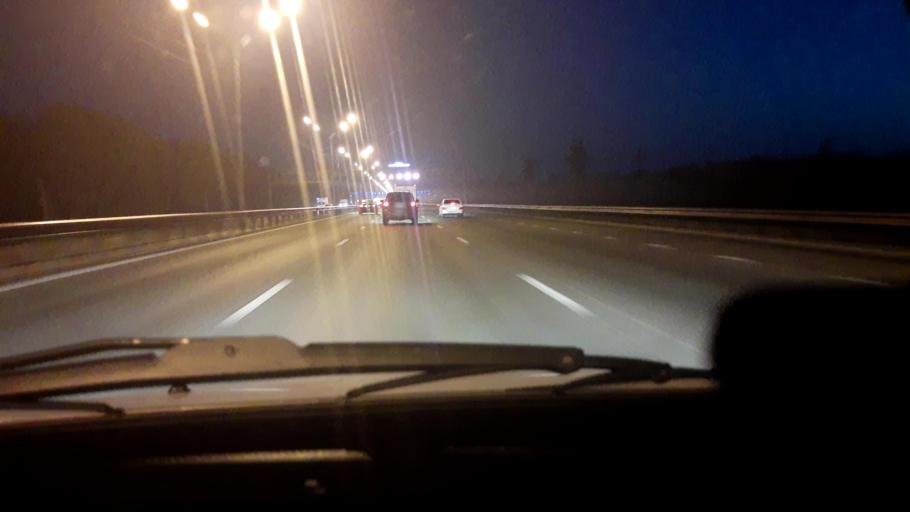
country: RU
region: Bashkortostan
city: Ufa
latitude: 54.6507
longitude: 55.9328
